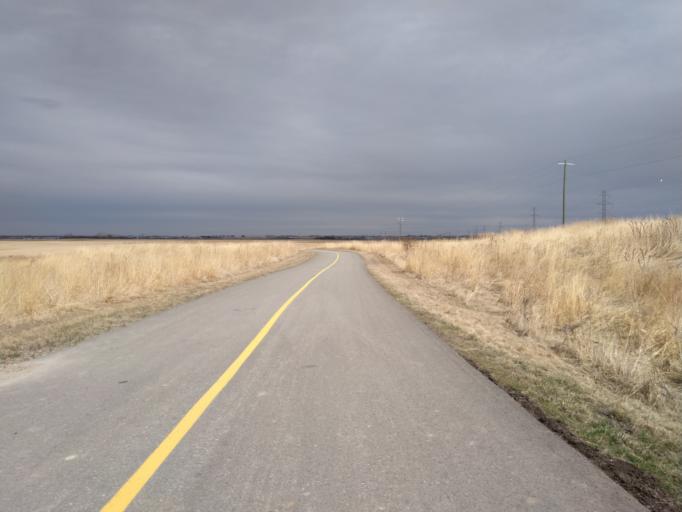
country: CA
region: Alberta
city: Airdrie
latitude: 51.1776
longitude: -114.0446
